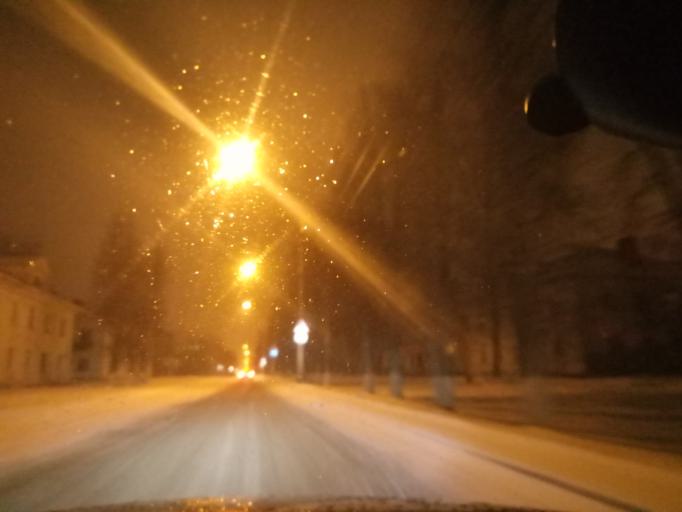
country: RU
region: Tula
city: Novomoskovsk
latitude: 54.0075
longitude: 38.2873
